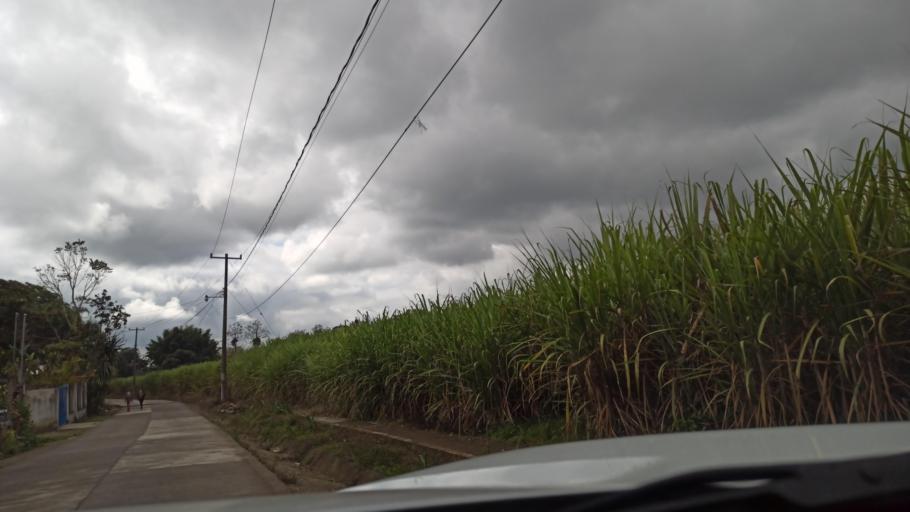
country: MX
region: Veracruz
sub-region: Chocaman
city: San Jose Neria
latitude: 19.0065
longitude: -97.0042
